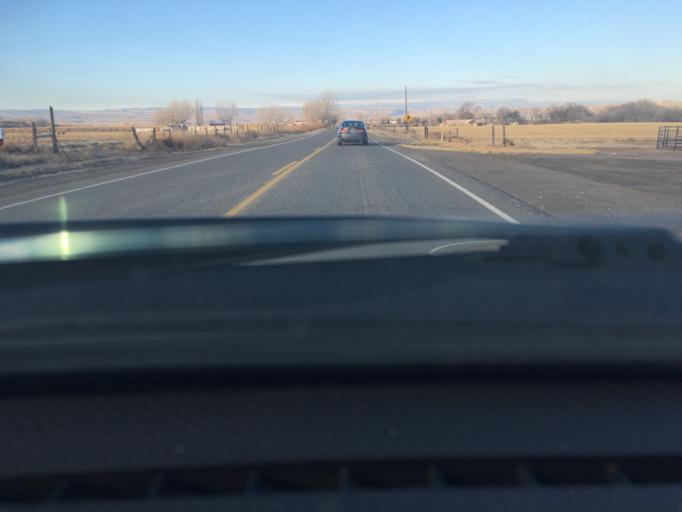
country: US
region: Colorado
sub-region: Delta County
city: Delta
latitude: 38.7410
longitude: -108.1069
